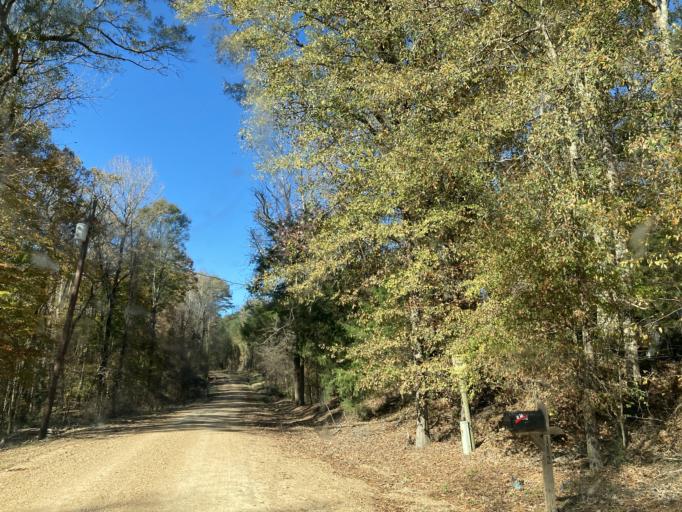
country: US
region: Mississippi
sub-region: Hinds County
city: Lynchburg
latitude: 32.5537
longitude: -90.5016
